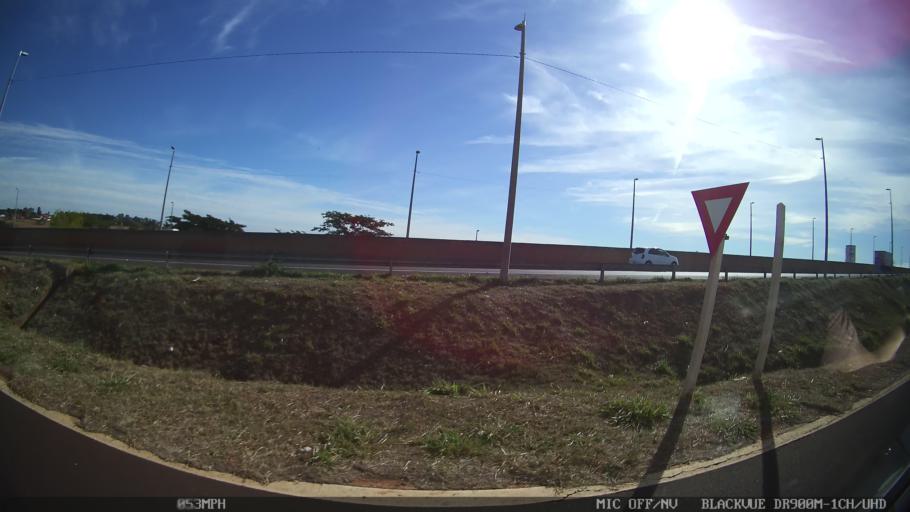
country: BR
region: Sao Paulo
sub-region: Sao Jose Do Rio Preto
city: Sao Jose do Rio Preto
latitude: -20.7369
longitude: -49.3373
